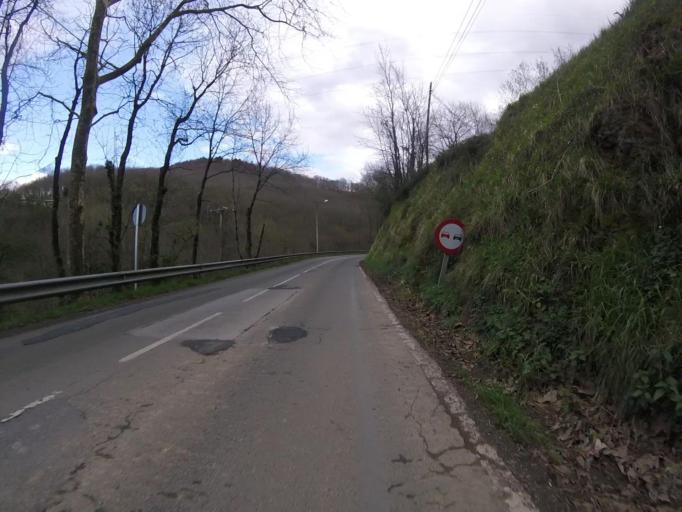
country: ES
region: Basque Country
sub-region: Provincia de Guipuzcoa
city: Errenteria
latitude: 43.2876
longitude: -1.8555
